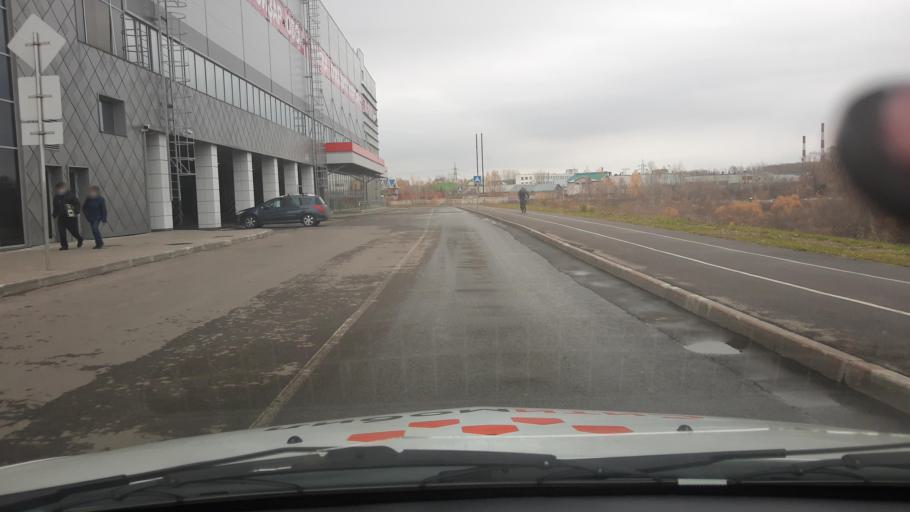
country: RU
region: Bashkortostan
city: Ufa
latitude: 54.7895
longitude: 56.0808
